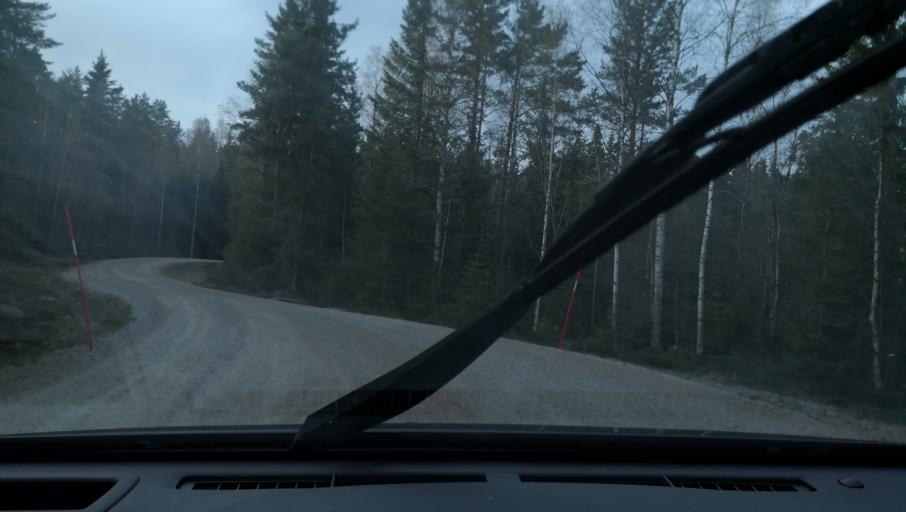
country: SE
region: Dalarna
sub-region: Saters Kommun
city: Saeter
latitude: 60.1772
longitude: 15.7254
